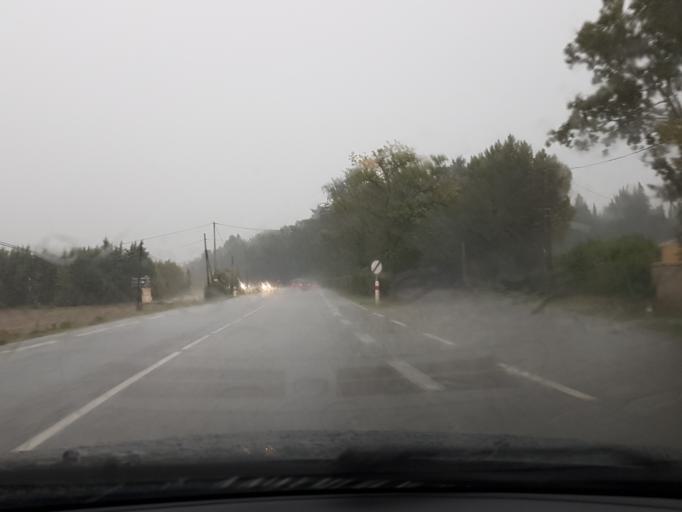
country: FR
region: Provence-Alpes-Cote d'Azur
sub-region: Departement du Vaucluse
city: Jonquerettes
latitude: 43.9627
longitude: 4.9498
